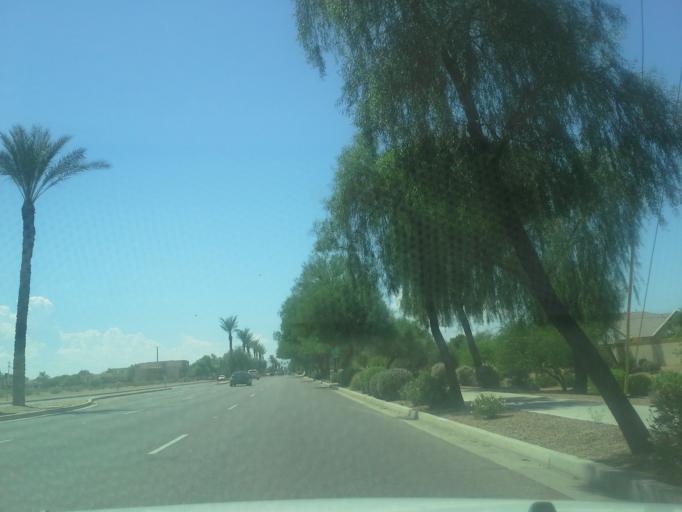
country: US
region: Arizona
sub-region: Maricopa County
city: Glendale
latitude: 33.5383
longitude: -112.2075
